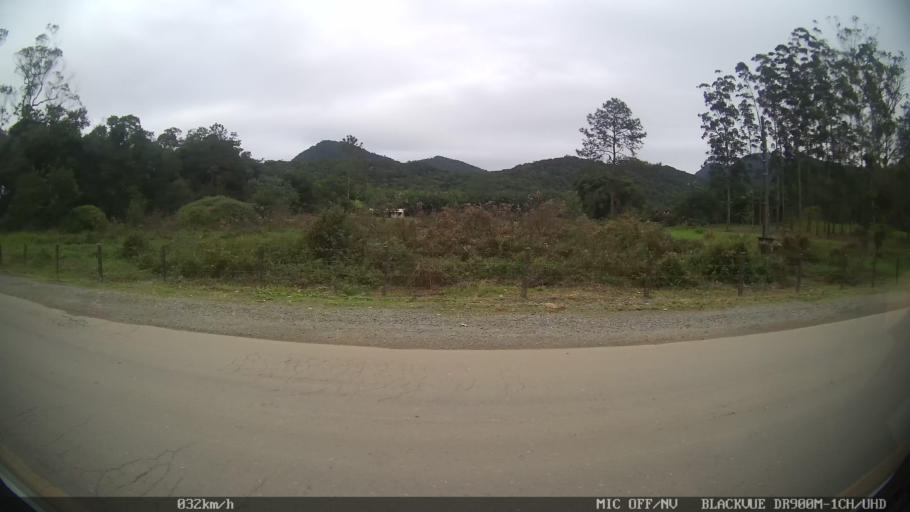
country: BR
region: Santa Catarina
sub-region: Joinville
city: Joinville
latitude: -26.2545
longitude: -48.9249
